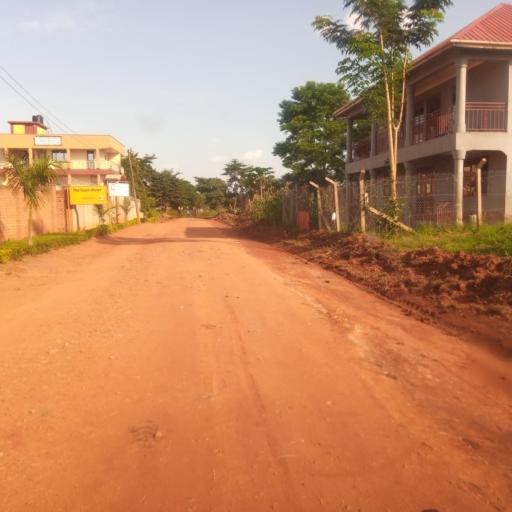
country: UG
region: Northern Region
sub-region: Kitgum District
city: Kitgum
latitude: 3.2902
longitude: 32.8851
